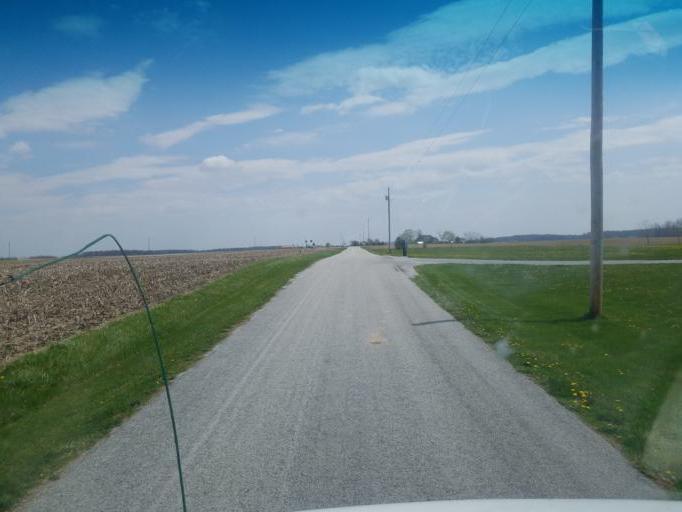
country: US
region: Ohio
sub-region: Hardin County
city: Forest
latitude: 40.7743
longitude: -83.4663
